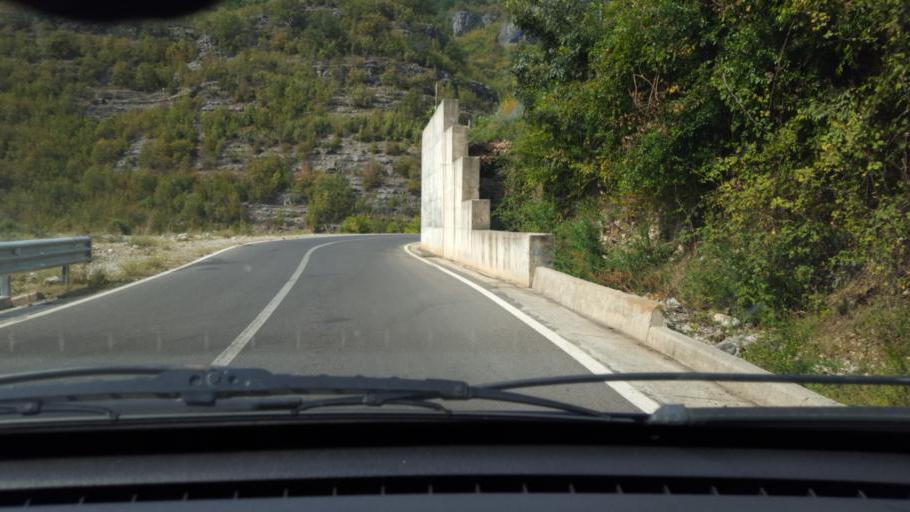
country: AL
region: Shkoder
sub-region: Rrethi i Malesia e Madhe
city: Kastrat
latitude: 42.4288
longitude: 19.5338
